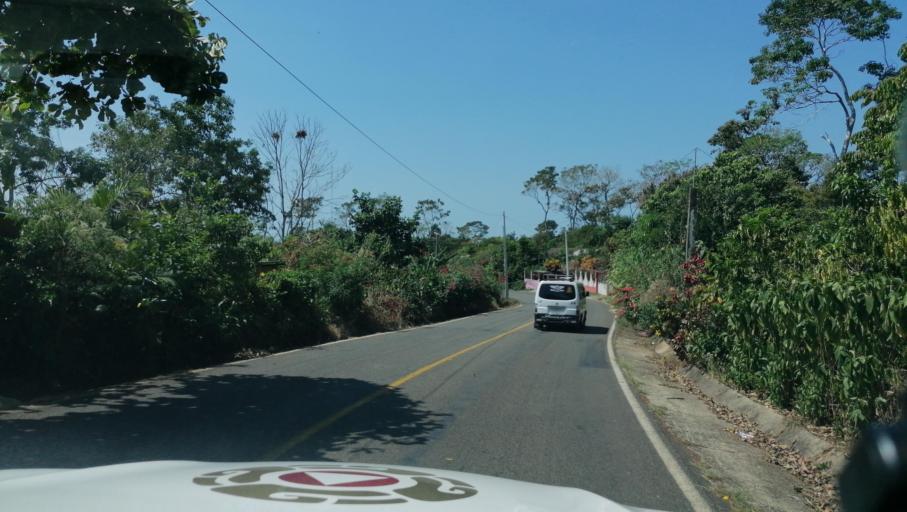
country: MX
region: Chiapas
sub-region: Cacahoatan
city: Benito Juarez
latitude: 15.0150
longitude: -92.2265
